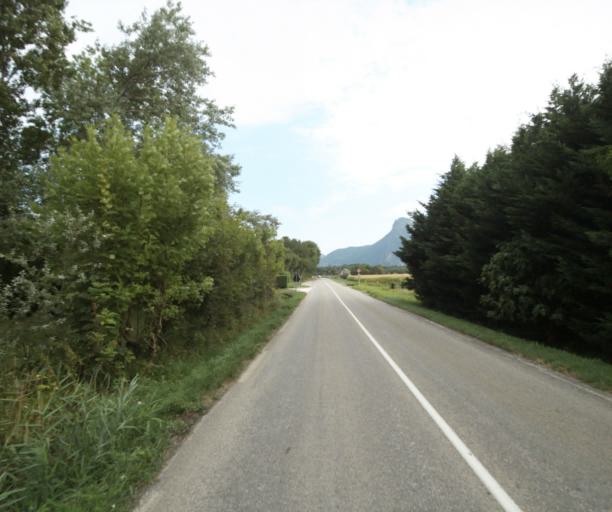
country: FR
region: Rhone-Alpes
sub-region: Departement de l'Isere
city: Noyarey
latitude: 45.2448
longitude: 5.6325
